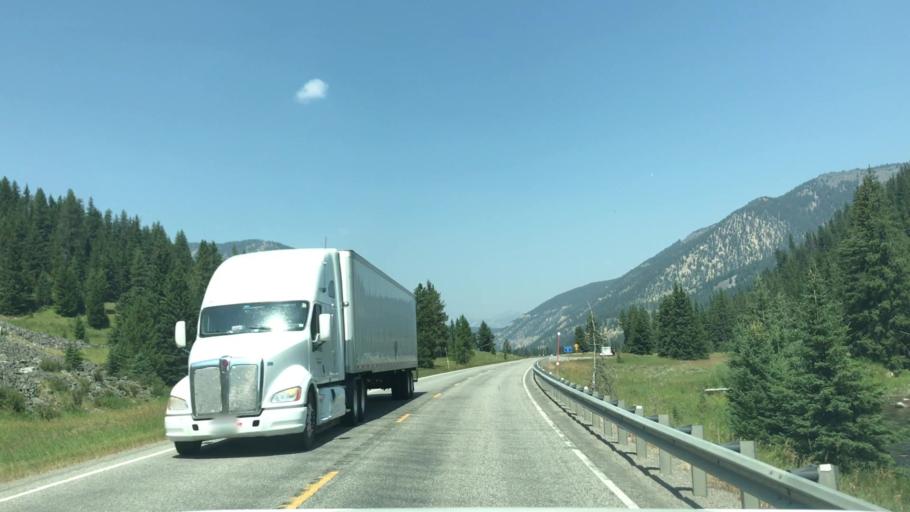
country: US
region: Montana
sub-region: Gallatin County
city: Big Sky
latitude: 45.0891
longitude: -111.2130
